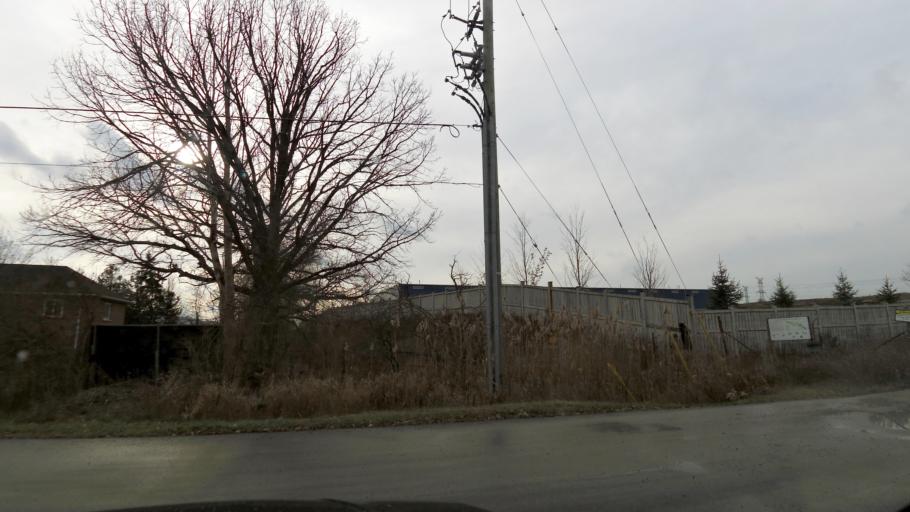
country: CA
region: Ontario
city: Etobicoke
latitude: 43.7469
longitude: -79.6527
